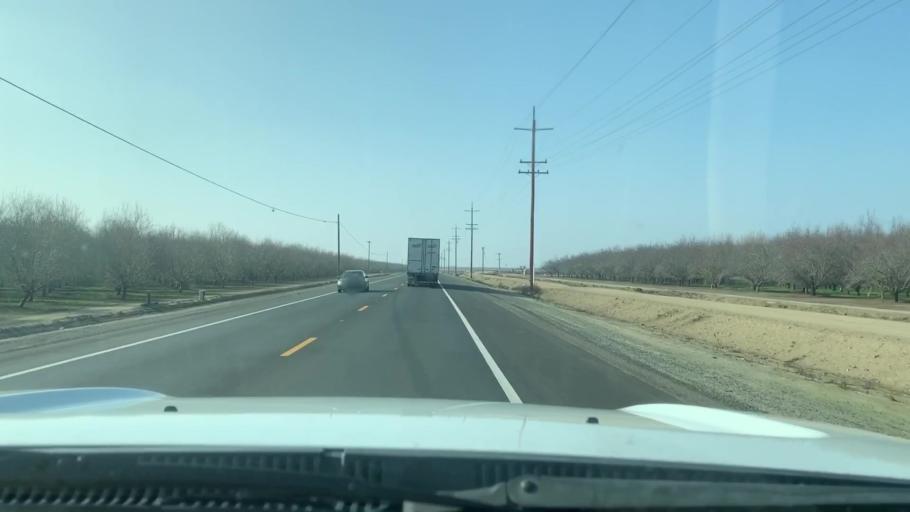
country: US
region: California
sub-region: Kern County
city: Wasco
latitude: 35.6017
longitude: -119.2919
